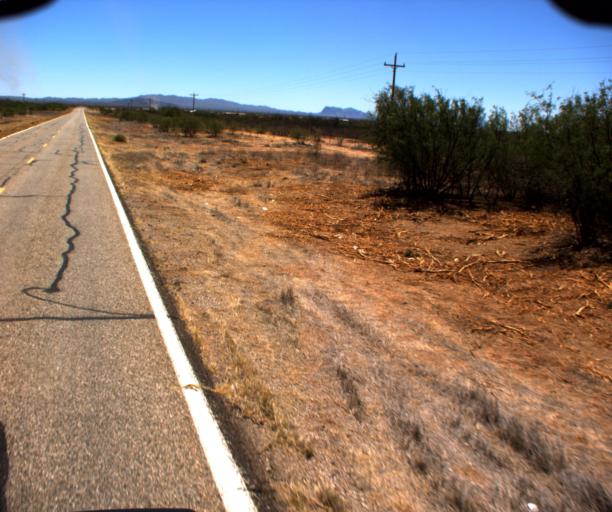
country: US
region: Arizona
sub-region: Pima County
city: Ajo
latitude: 32.1860
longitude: -112.3767
